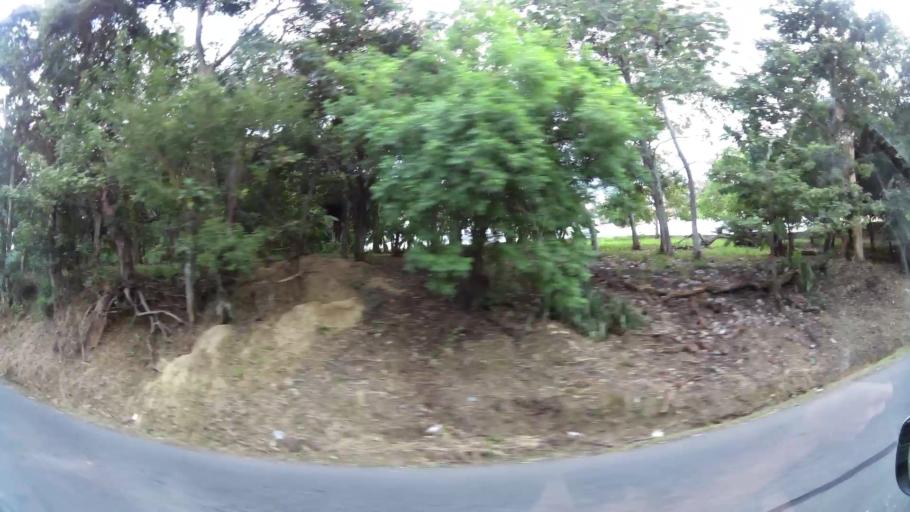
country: CR
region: San Jose
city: Santa Ana
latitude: 9.9319
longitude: -84.1710
